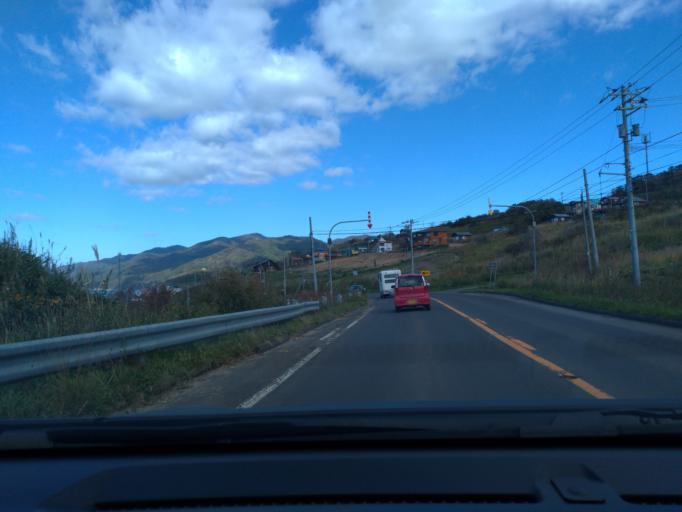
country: JP
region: Hokkaido
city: Ishikari
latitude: 43.3900
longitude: 141.4334
